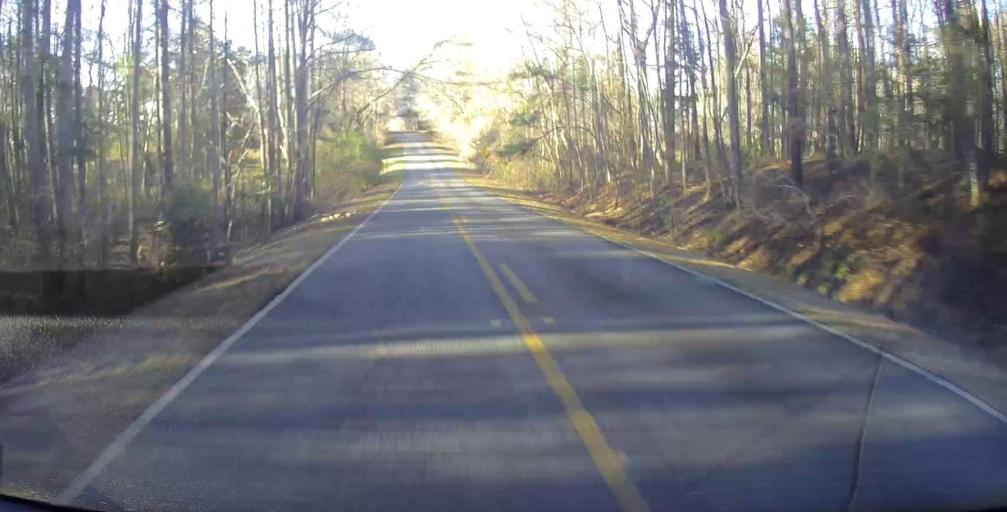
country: US
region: Georgia
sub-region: Meriwether County
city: Manchester
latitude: 32.9107
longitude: -84.6100
